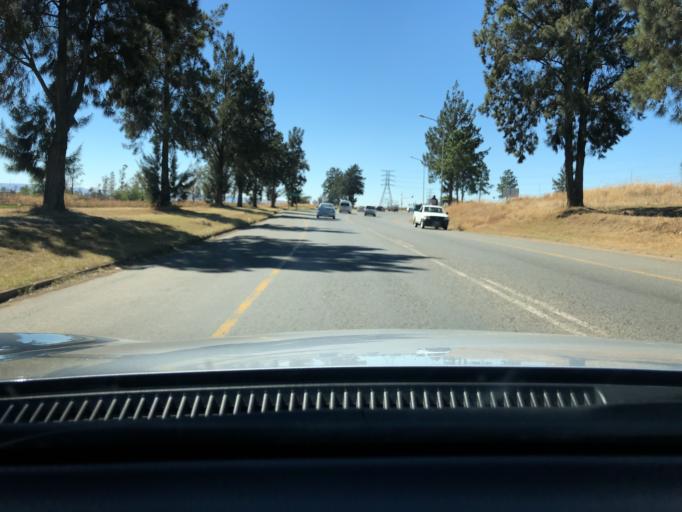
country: ZA
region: KwaZulu-Natal
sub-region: Amajuba District Municipality
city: Newcastle
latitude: -27.7611
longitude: 29.9594
